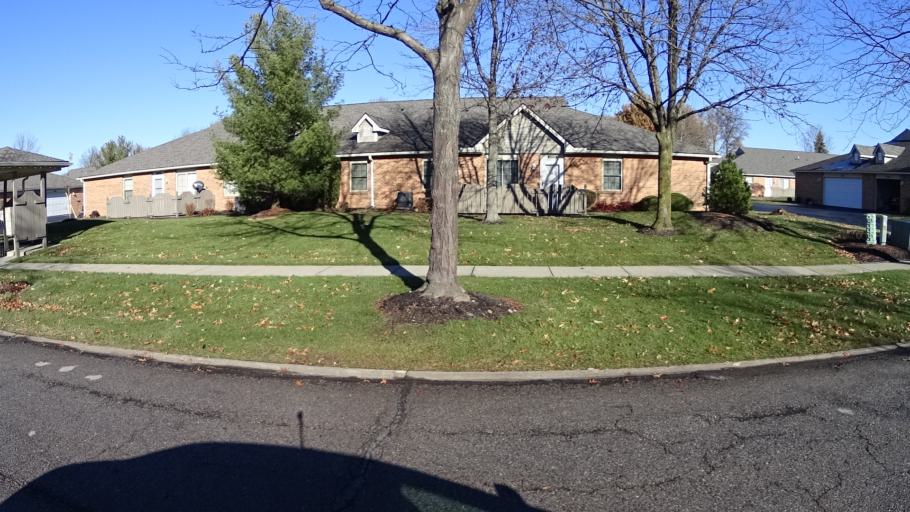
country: US
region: Ohio
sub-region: Lorain County
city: North Ridgeville
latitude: 41.4179
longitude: -82.0098
